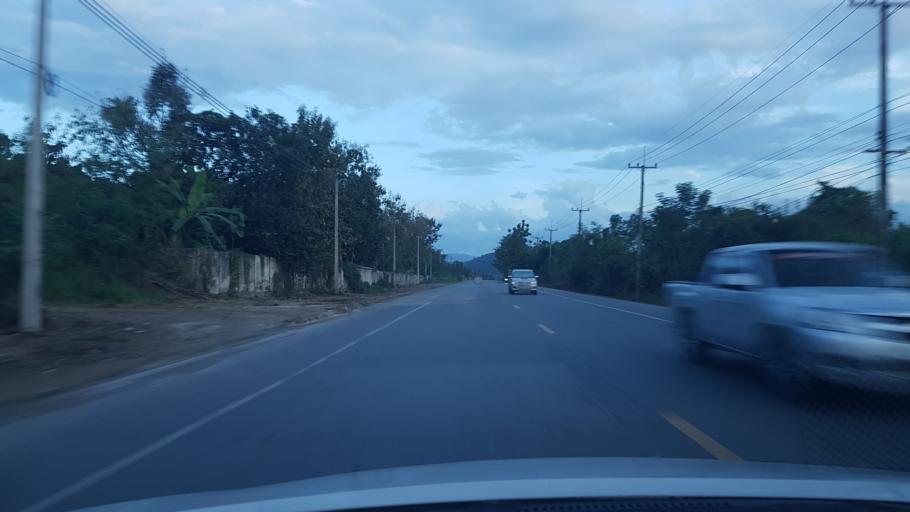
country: TH
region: Sara Buri
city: Kaeng Khoi
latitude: 14.4788
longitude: 101.0552
